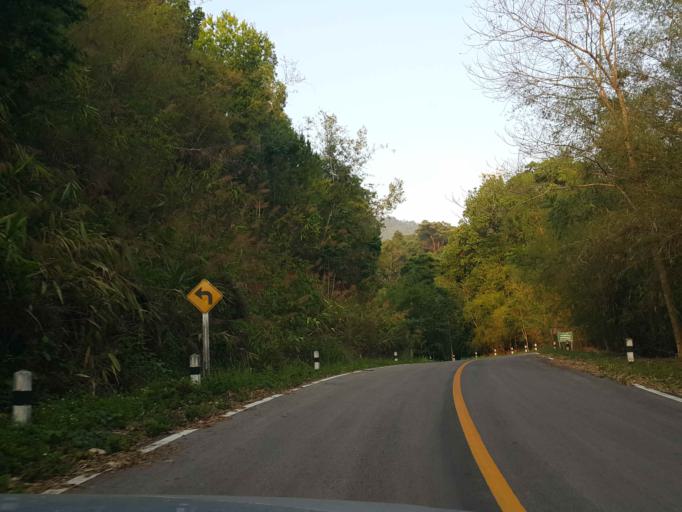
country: TH
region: Chiang Mai
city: Mae On
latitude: 18.9801
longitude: 99.3278
